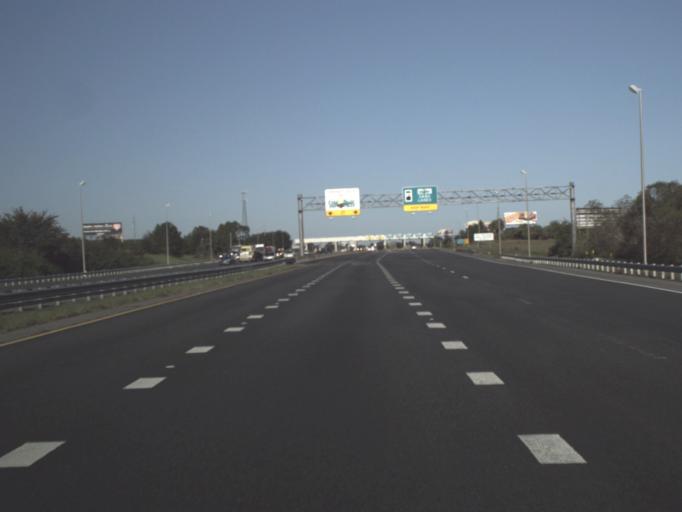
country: US
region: Florida
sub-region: Lake County
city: Yalaha
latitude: 28.6668
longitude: -81.8363
